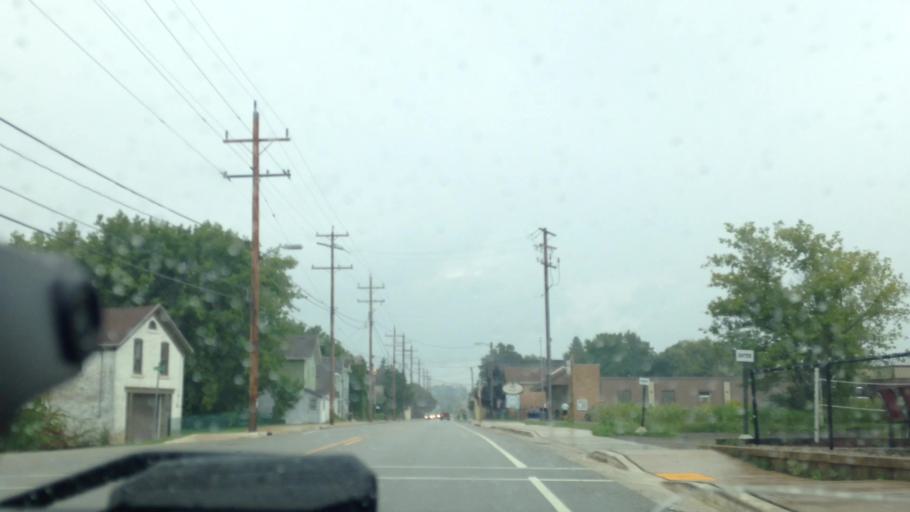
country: US
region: Wisconsin
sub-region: Washington County
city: Richfield
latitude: 43.2584
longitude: -88.1956
